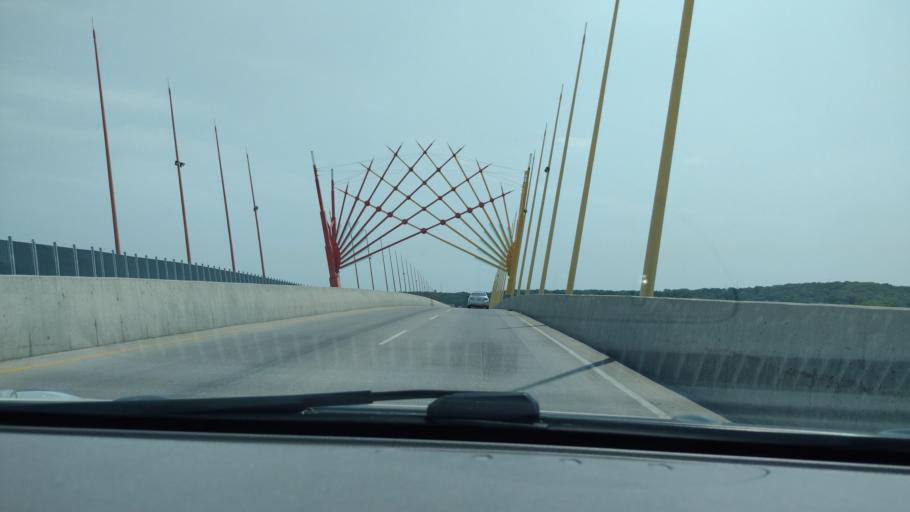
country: US
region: Iowa
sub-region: Pottawattamie County
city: Council Bluffs
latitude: 41.2618
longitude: -95.8628
